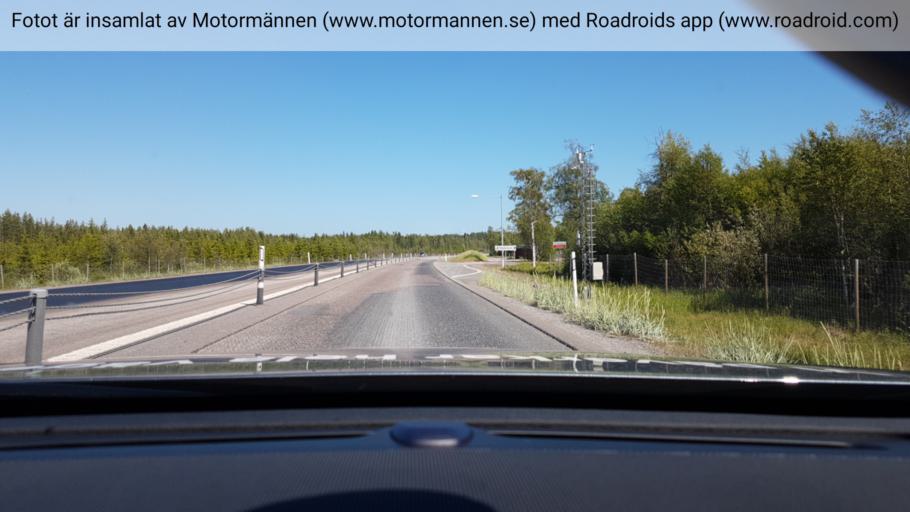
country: SE
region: Vaesterbotten
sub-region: Nordmalings Kommun
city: Nordmaling
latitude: 63.5714
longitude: 19.4392
